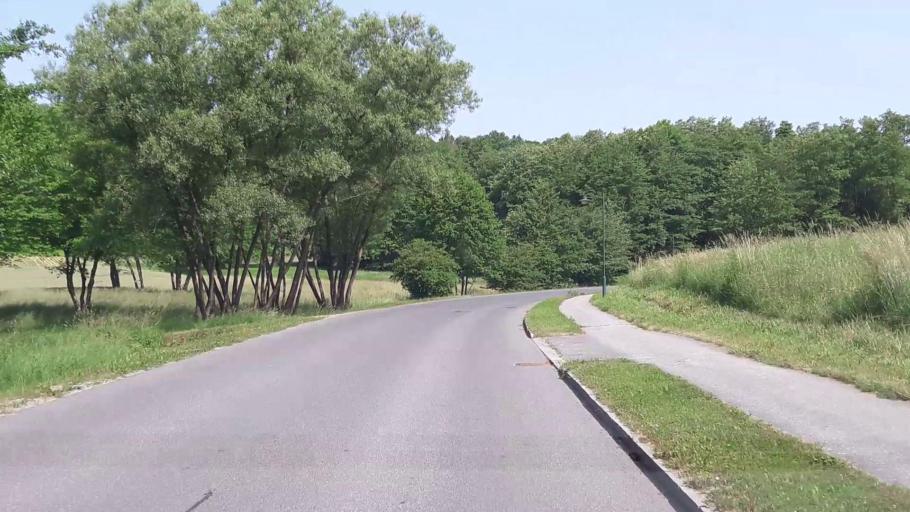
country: AT
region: Burgenland
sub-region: Politischer Bezirk Gussing
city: Stegersbach
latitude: 47.1667
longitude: 16.1490
